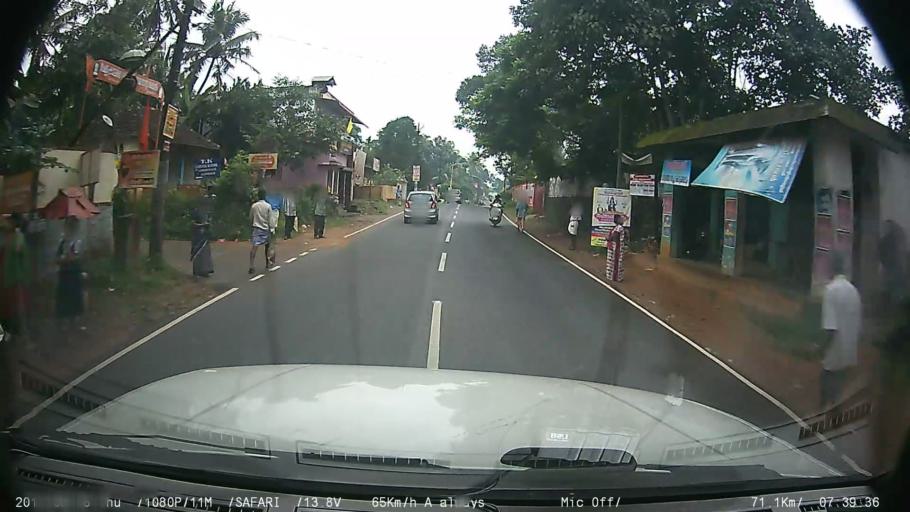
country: IN
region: Kerala
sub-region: Kottayam
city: Changanacheri
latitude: 9.4475
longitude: 76.5725
